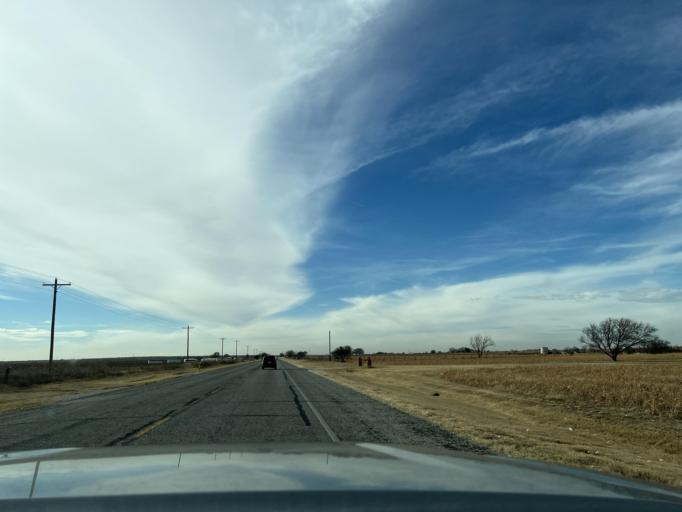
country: US
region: Texas
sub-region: Fisher County
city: Roby
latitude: 32.7574
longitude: -100.2792
